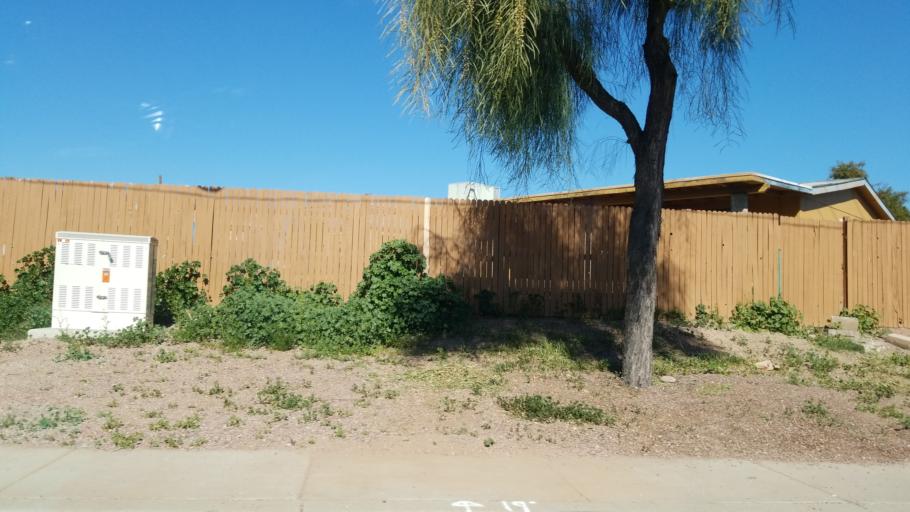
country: US
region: Arizona
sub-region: Maricopa County
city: Glendale
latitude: 33.6475
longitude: -112.0739
